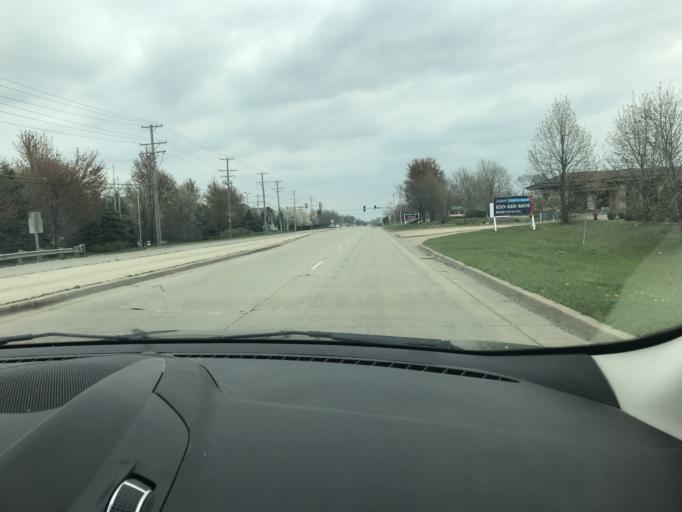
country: US
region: Illinois
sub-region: Kane County
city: Aurora
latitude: 41.7212
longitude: -88.2778
